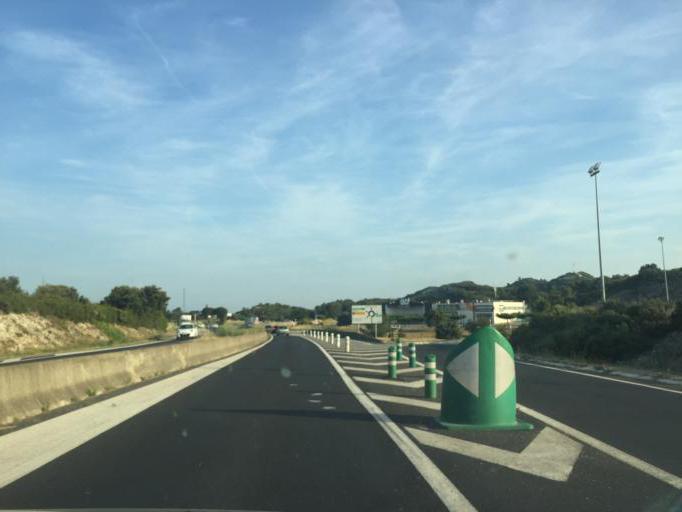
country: FR
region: Languedoc-Roussillon
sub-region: Departement du Gard
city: Les Angles
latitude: 43.9614
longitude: 4.7452
